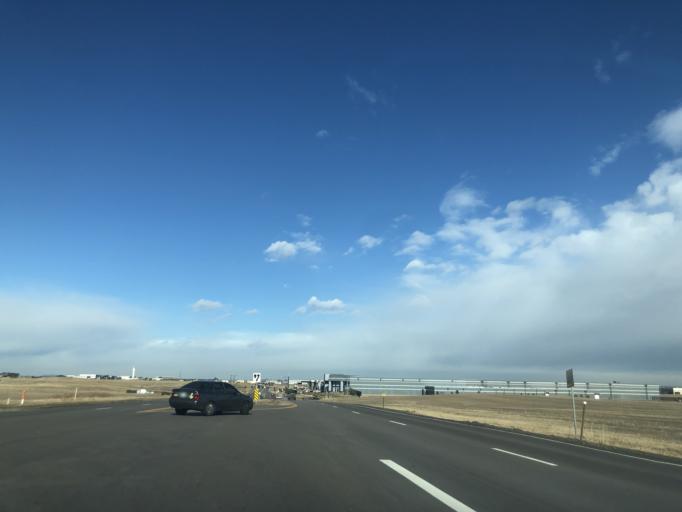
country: US
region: Colorado
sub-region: Douglas County
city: Meridian
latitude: 39.5552
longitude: -104.8393
